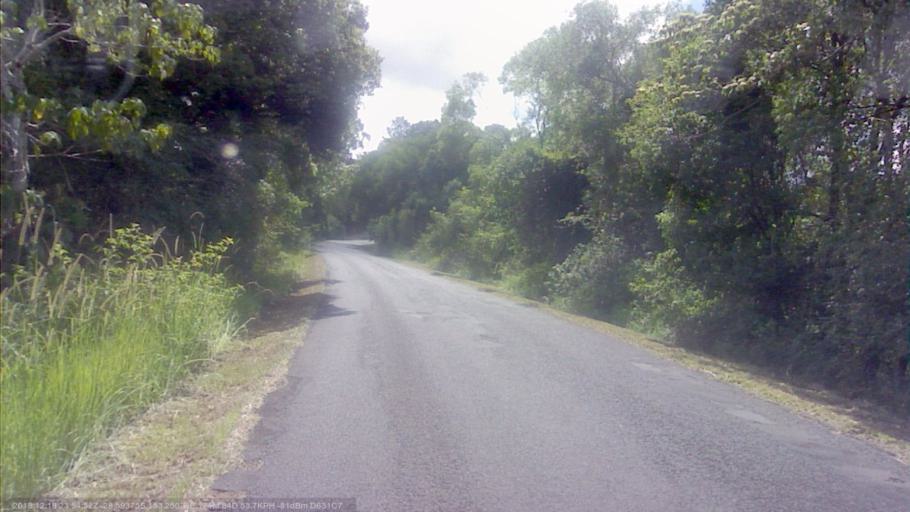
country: AU
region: New South Wales
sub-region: Lismore Municipality
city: Nimbin
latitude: -28.5937
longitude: 153.2502
